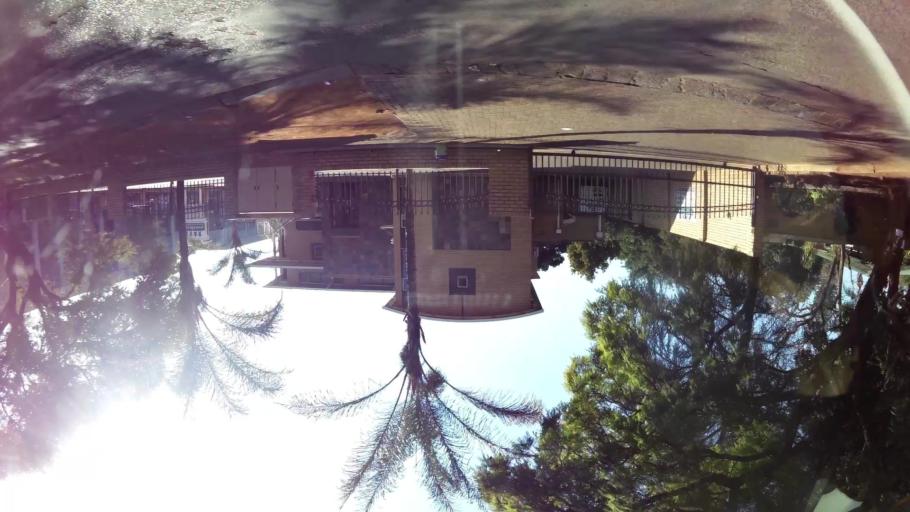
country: ZA
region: Gauteng
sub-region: City of Tshwane Metropolitan Municipality
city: Pretoria
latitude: -25.6778
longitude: 28.1723
